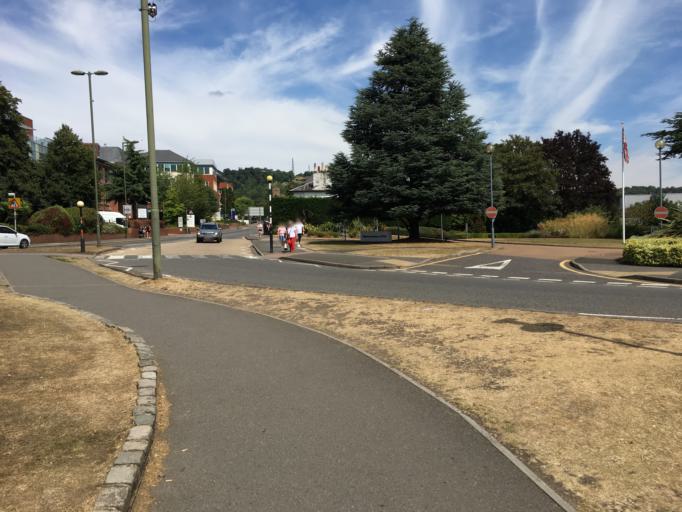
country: GB
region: England
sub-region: Surrey
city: Reigate
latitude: 51.2401
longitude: -0.2055
